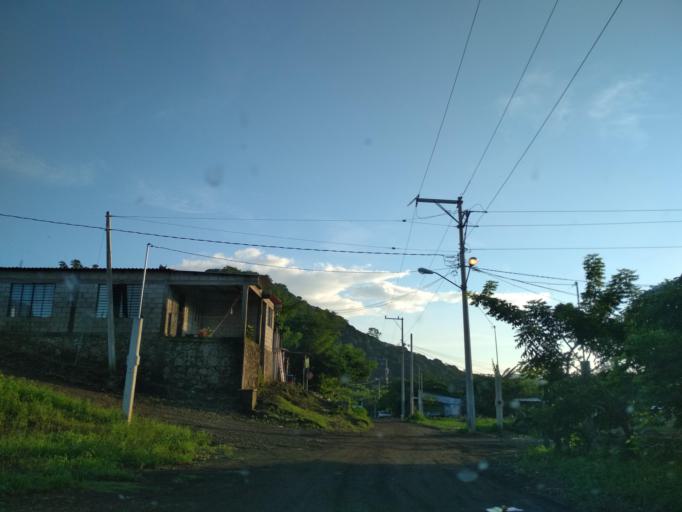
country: MX
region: Veracruz
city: Catemaco
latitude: 18.4219
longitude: -95.1238
